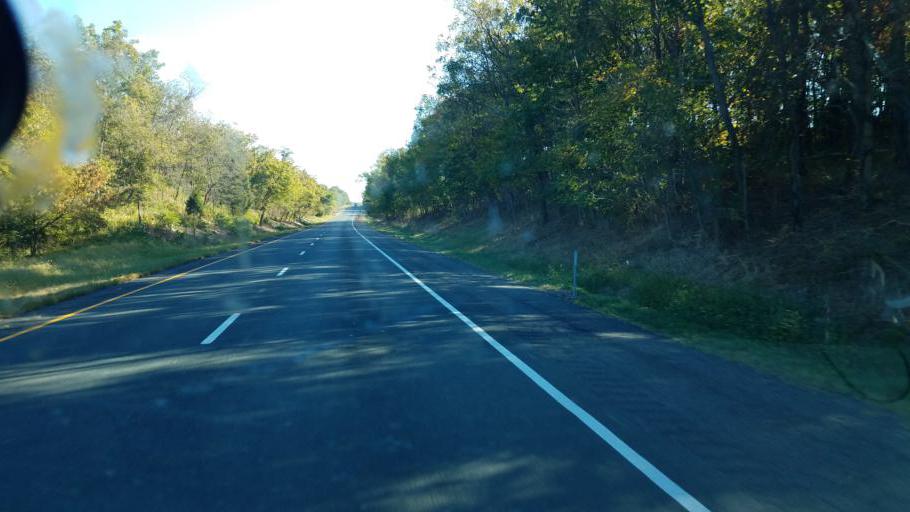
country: US
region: Maryland
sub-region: Washington County
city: Wilson-Conococheague
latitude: 39.6362
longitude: -77.9555
